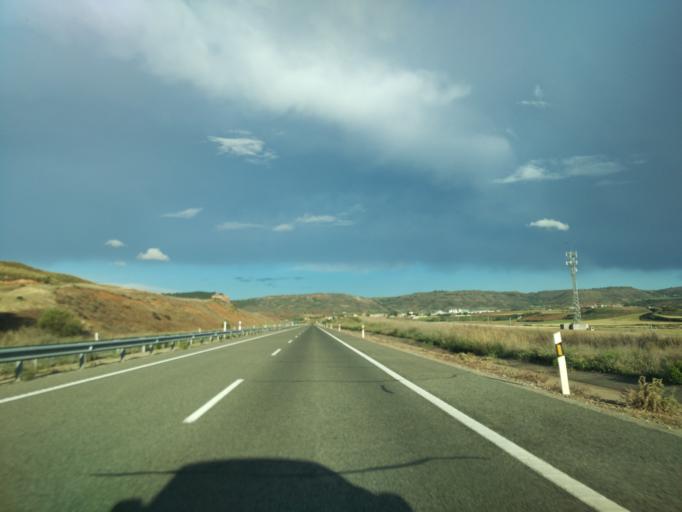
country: ES
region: Castille-La Mancha
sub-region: Provincia de Guadalajara
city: Guadalajara
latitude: 40.6635
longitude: -3.1514
